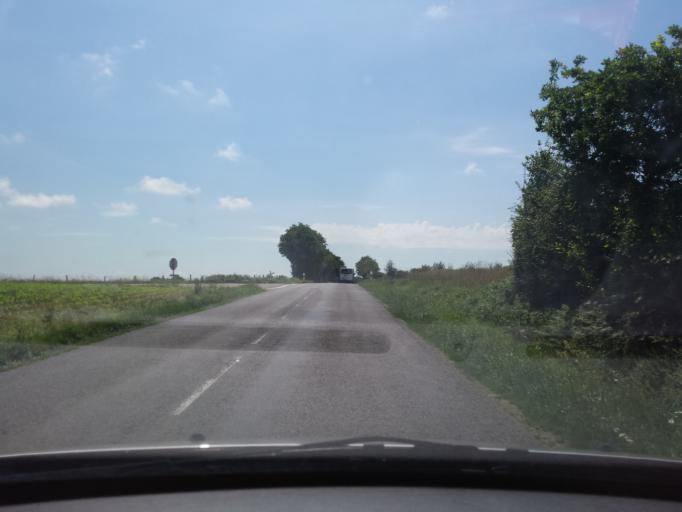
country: FR
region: Pays de la Loire
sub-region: Departement de la Loire-Atlantique
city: Saint-Pere-en-Retz
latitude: 47.1888
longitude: -2.0578
